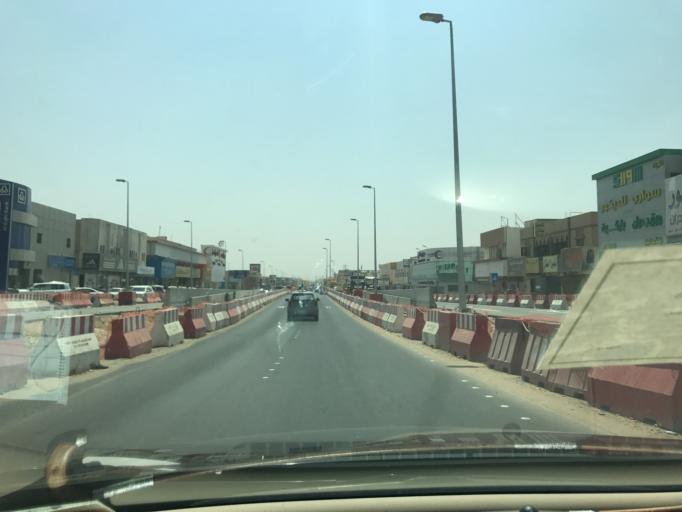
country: SA
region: Ar Riyad
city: Riyadh
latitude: 24.7520
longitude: 46.7709
